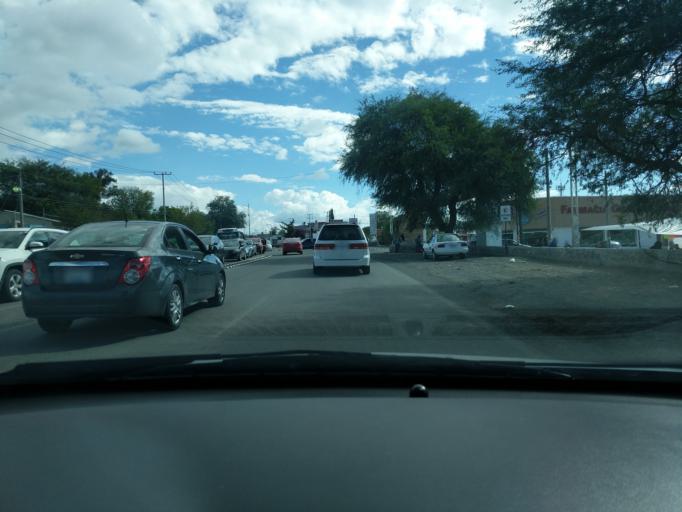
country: MX
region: Queretaro
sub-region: El Marques
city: General Lazaro Cardenas (El Colorado)
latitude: 20.5810
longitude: -100.2540
